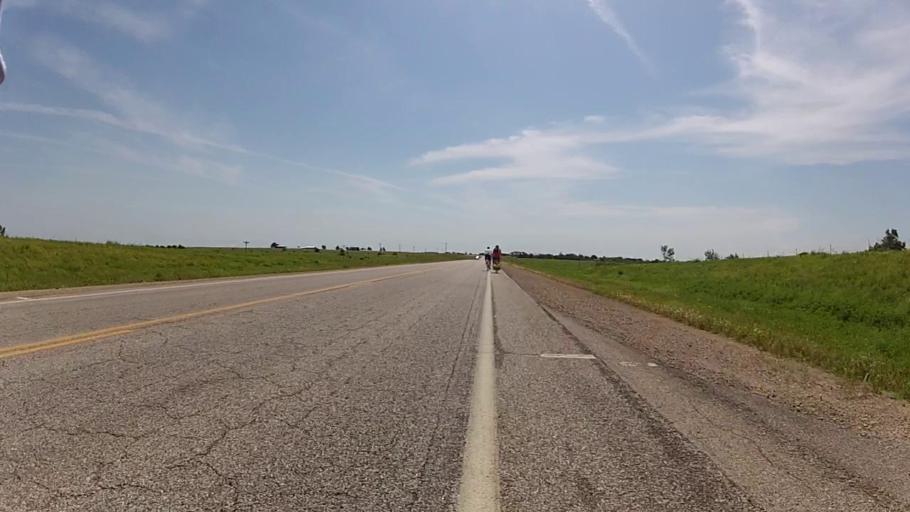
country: US
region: Kansas
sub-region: Chautauqua County
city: Sedan
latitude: 37.1101
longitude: -96.5245
